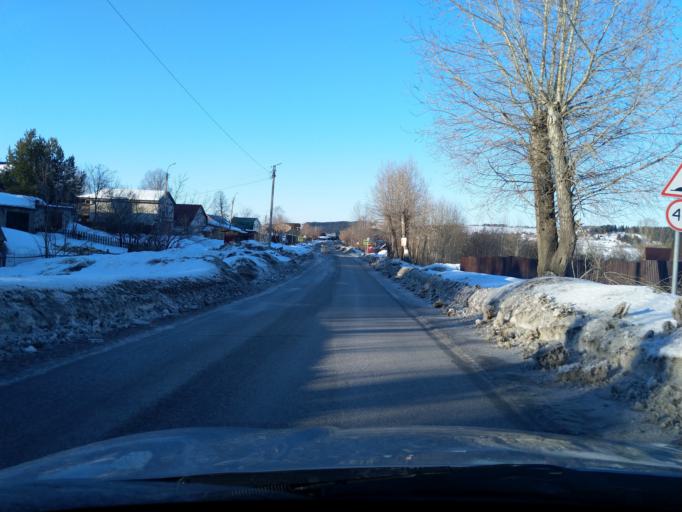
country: RU
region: Perm
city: Polazna
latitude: 58.2947
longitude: 56.4159
